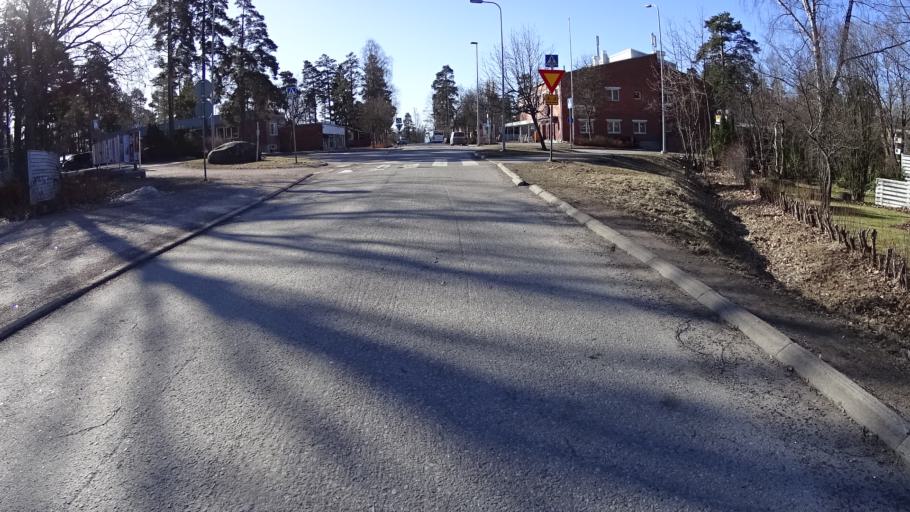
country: FI
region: Uusimaa
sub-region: Helsinki
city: Kilo
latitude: 60.2048
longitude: 24.8051
